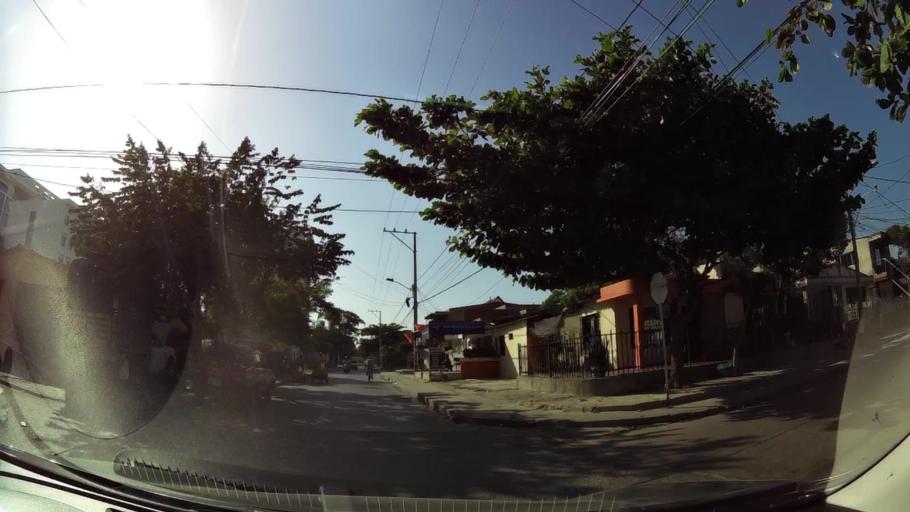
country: CO
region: Bolivar
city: Cartagena
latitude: 10.4079
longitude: -75.5038
